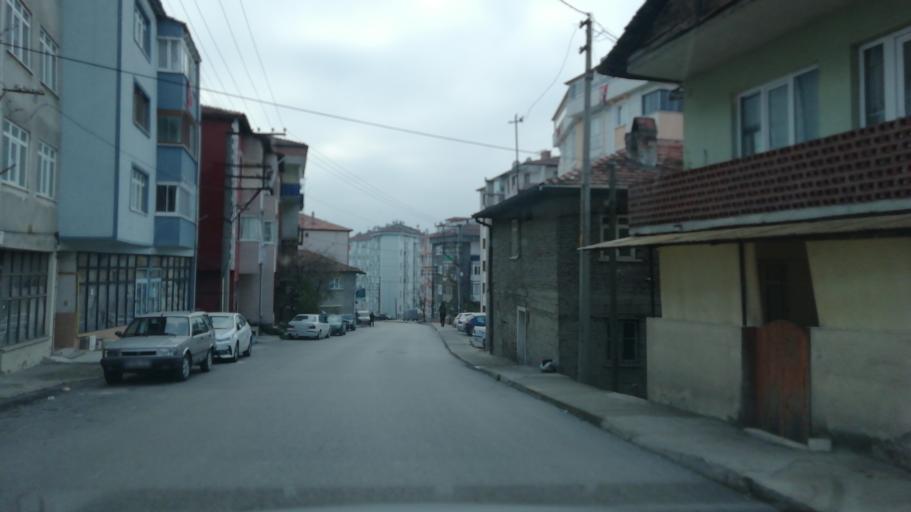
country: TR
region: Karabuk
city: Karabuk
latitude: 41.2088
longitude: 32.6271
